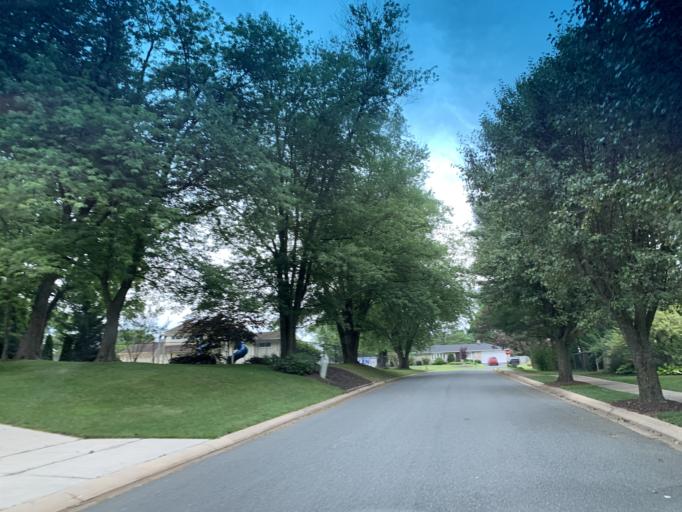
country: US
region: Maryland
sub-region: Harford County
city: Bel Air
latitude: 39.5197
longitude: -76.3548
